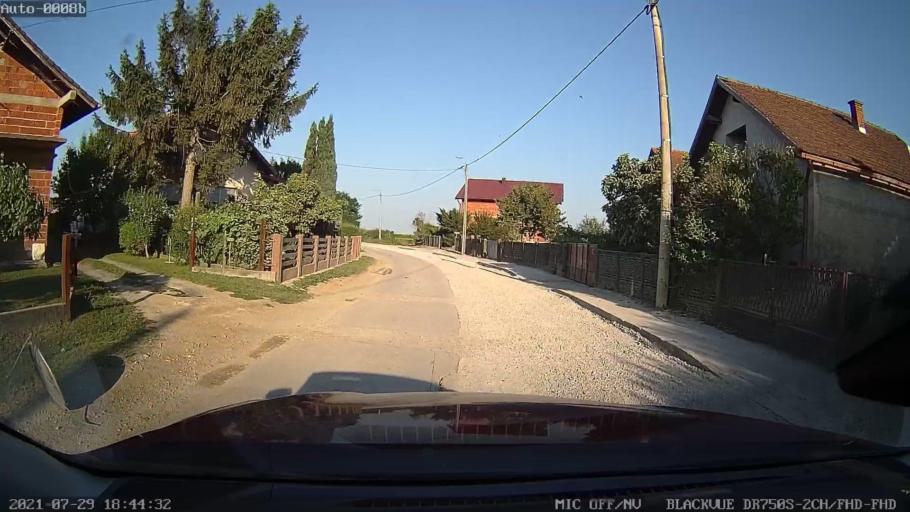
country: HR
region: Varazdinska
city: Petrijanec
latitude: 46.3164
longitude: 16.2384
